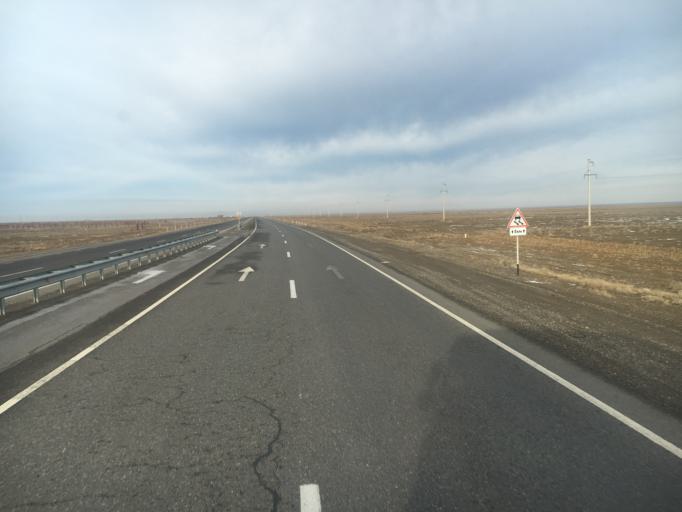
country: KZ
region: Ongtustik Qazaqstan
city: Turkestan
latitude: 43.5019
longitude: 67.8432
